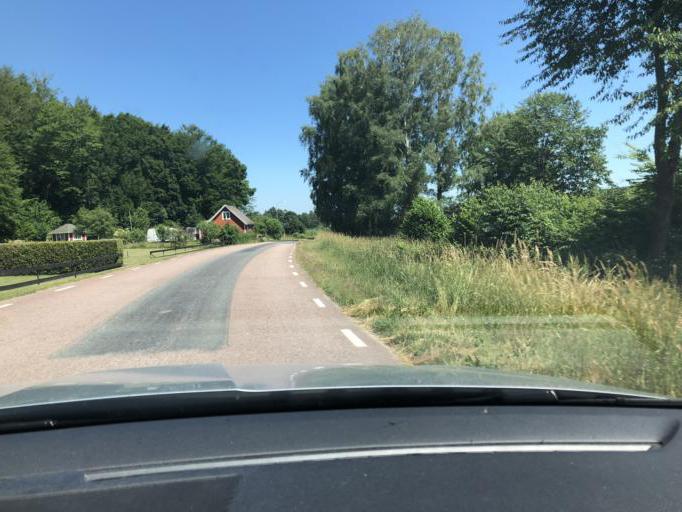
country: SE
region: Blekinge
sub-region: Olofstroms Kommun
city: Jamshog
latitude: 56.1679
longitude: 14.5998
